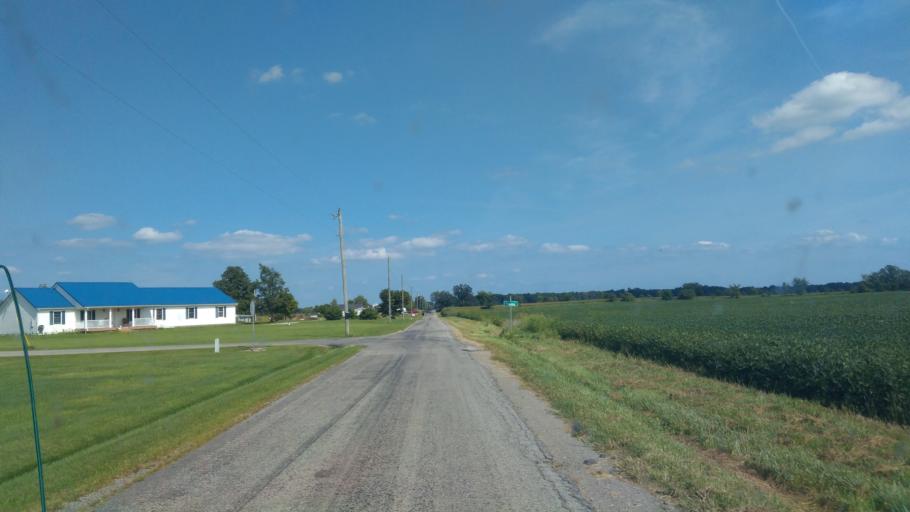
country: US
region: Ohio
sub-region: Union County
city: Richwood
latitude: 40.4678
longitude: -83.3902
